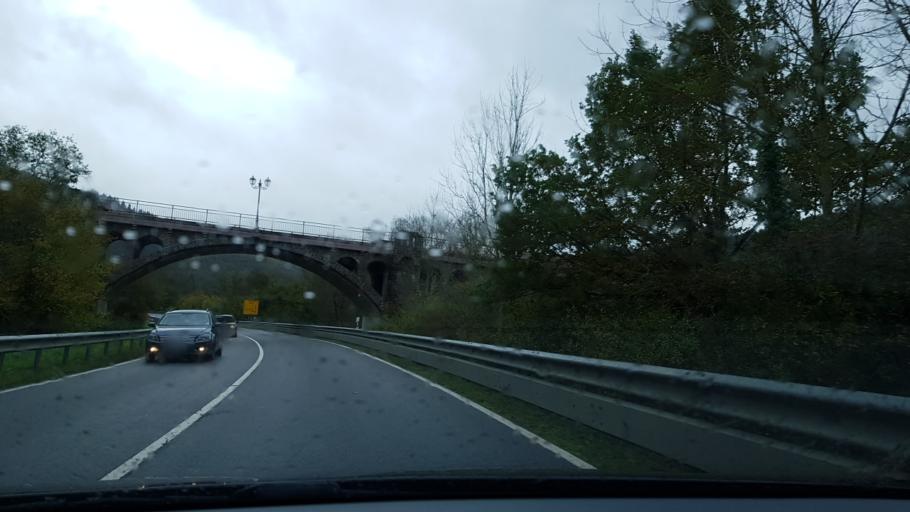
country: DE
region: Rheinland-Pfalz
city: Honningen
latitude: 50.4718
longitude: 6.9494
